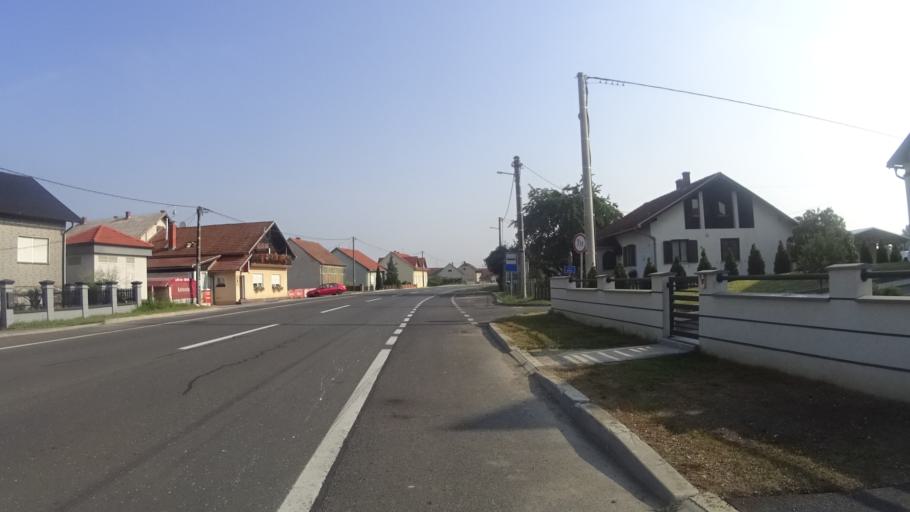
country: HR
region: Medimurska
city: Nedelisce
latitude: 46.3506
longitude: 16.3629
